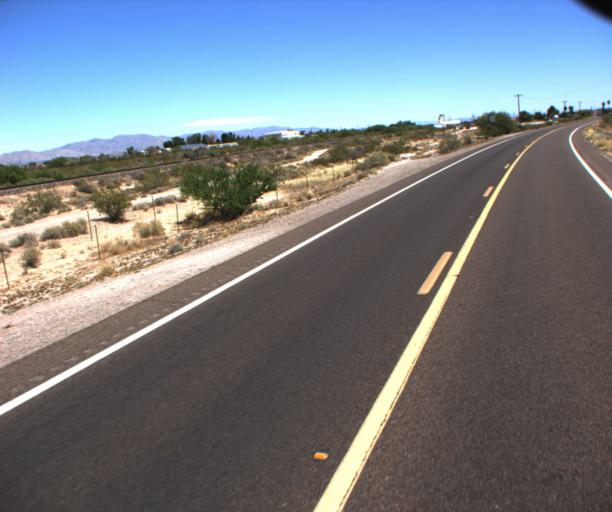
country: US
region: Arizona
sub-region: La Paz County
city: Salome
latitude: 33.7769
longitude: -113.6234
